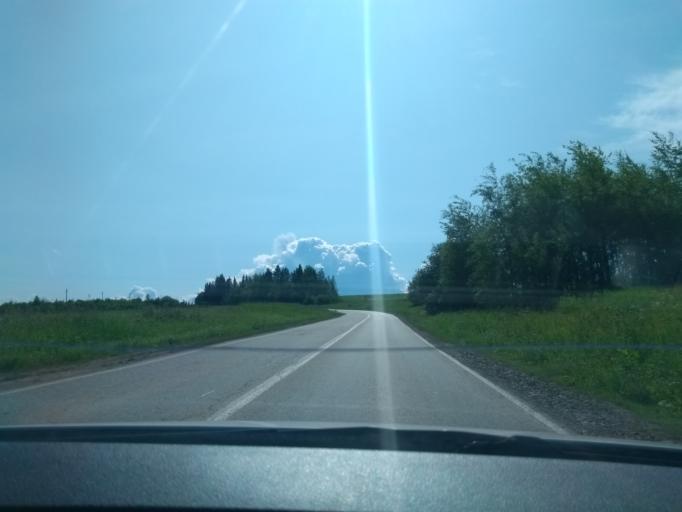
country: RU
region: Perm
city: Lobanovo
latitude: 57.8536
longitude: 56.3247
